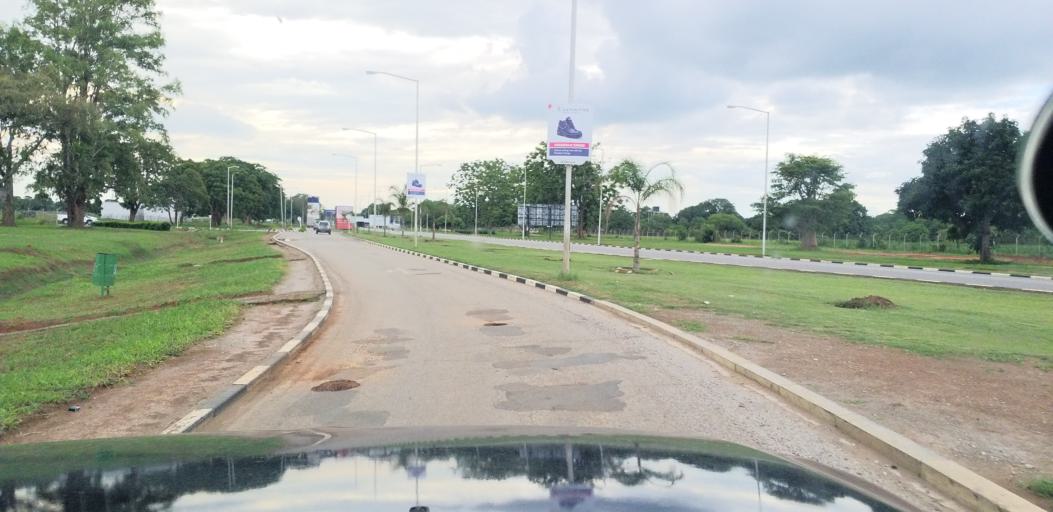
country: ZM
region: Lusaka
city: Lusaka
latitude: -15.3206
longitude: 28.4452
